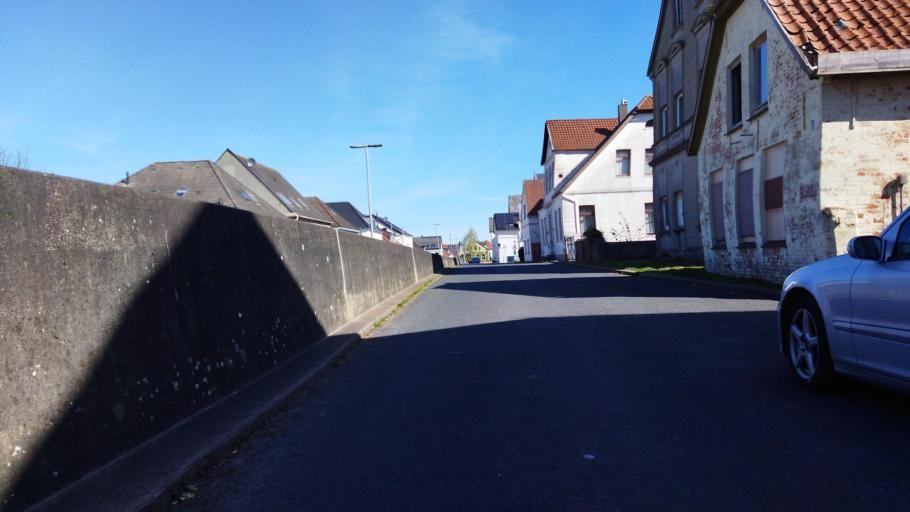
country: DE
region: Lower Saxony
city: Elsfleth
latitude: 53.2368
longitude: 8.4642
